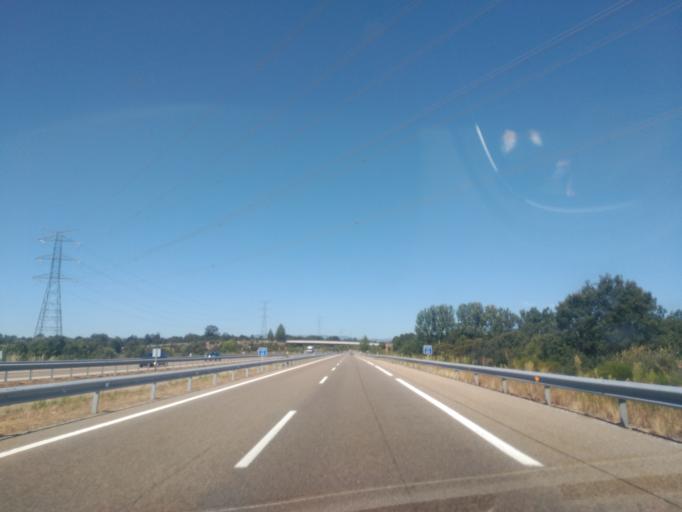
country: ES
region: Castille and Leon
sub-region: Provincia de Zamora
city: Cernadilla
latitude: 42.0290
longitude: -6.4145
